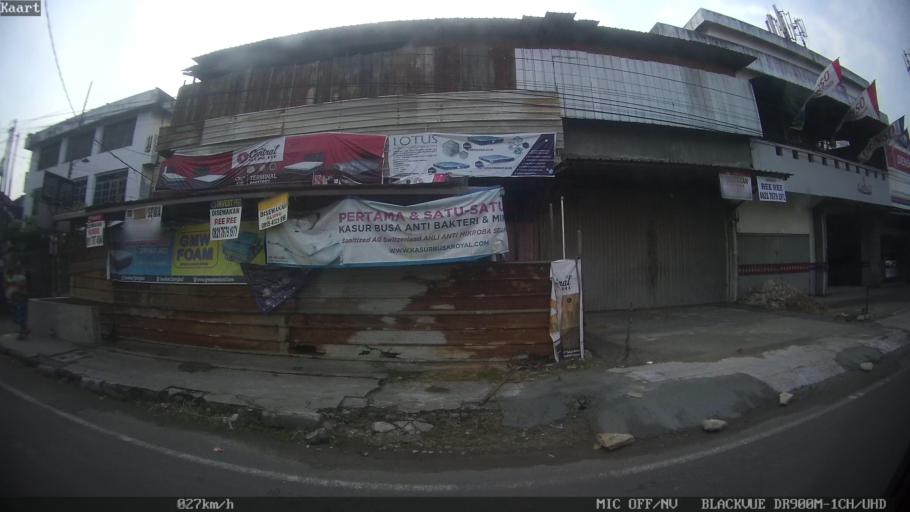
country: ID
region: Lampung
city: Bandarlampung
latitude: -5.4411
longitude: 105.2650
